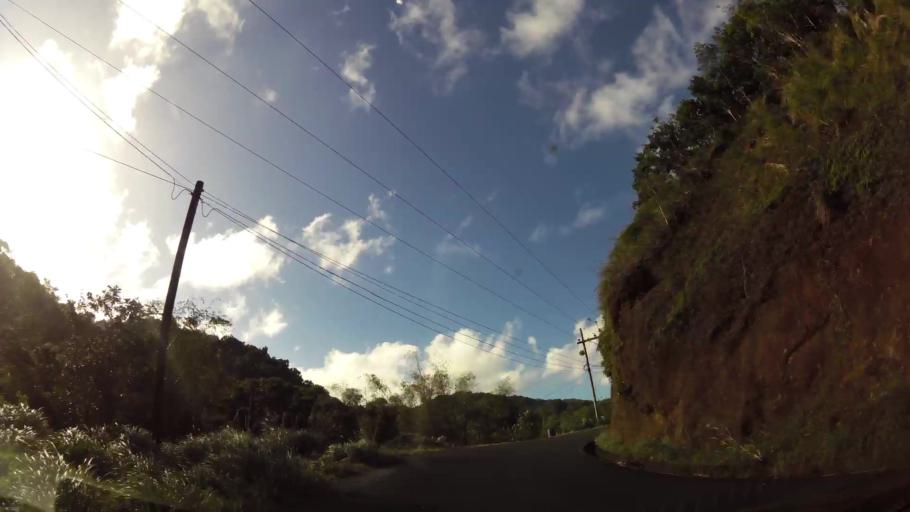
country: DM
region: Saint John
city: Portsmouth
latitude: 15.5825
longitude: -61.4150
